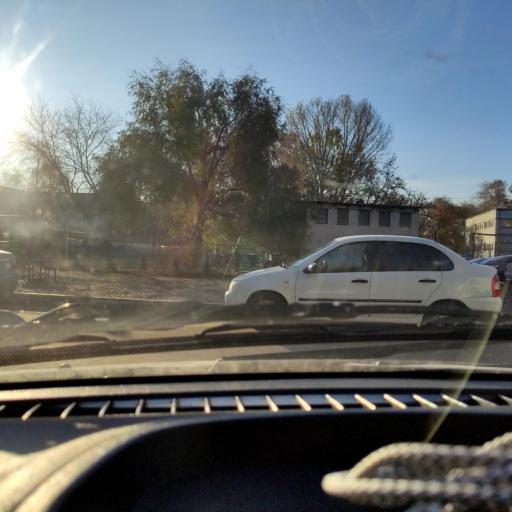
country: RU
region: Samara
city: Tol'yatti
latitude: 53.5282
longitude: 49.4006
